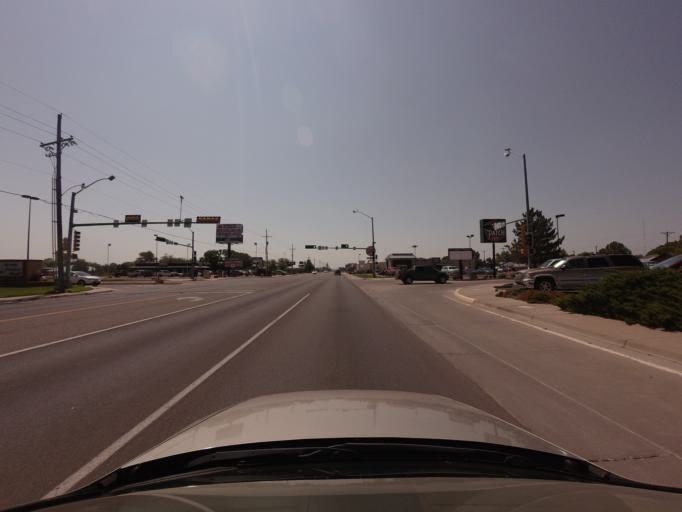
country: US
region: New Mexico
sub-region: Curry County
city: Clovis
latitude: 34.4247
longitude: -103.1966
